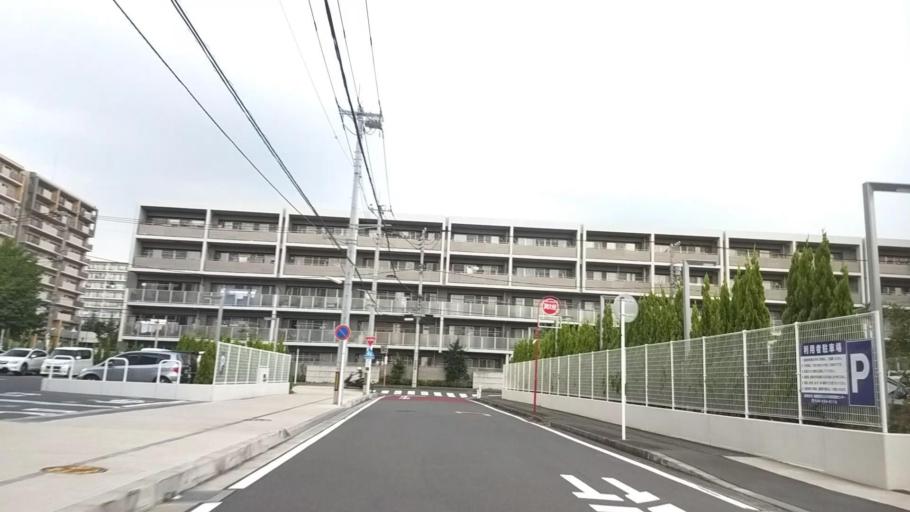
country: JP
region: Kanagawa
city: Atsugi
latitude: 35.4483
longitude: 139.3815
